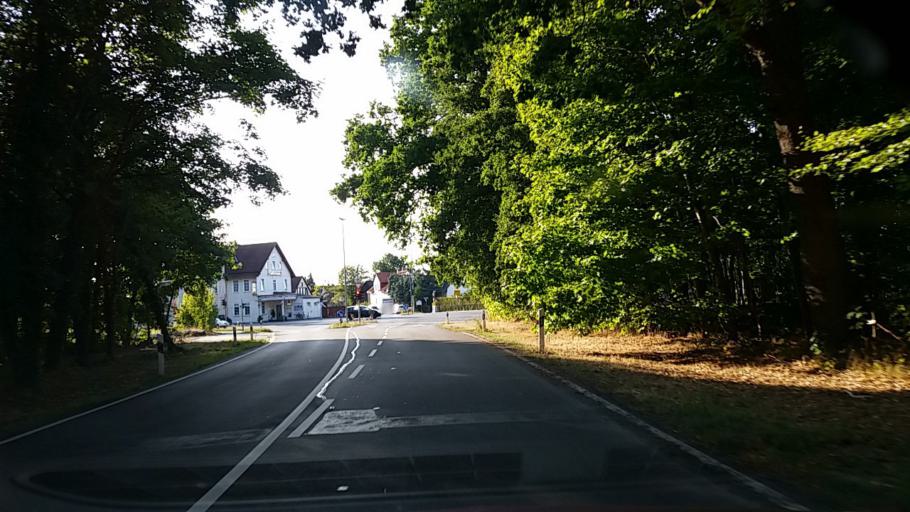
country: DE
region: Lower Saxony
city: Lehre
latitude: 52.3158
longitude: 10.6411
